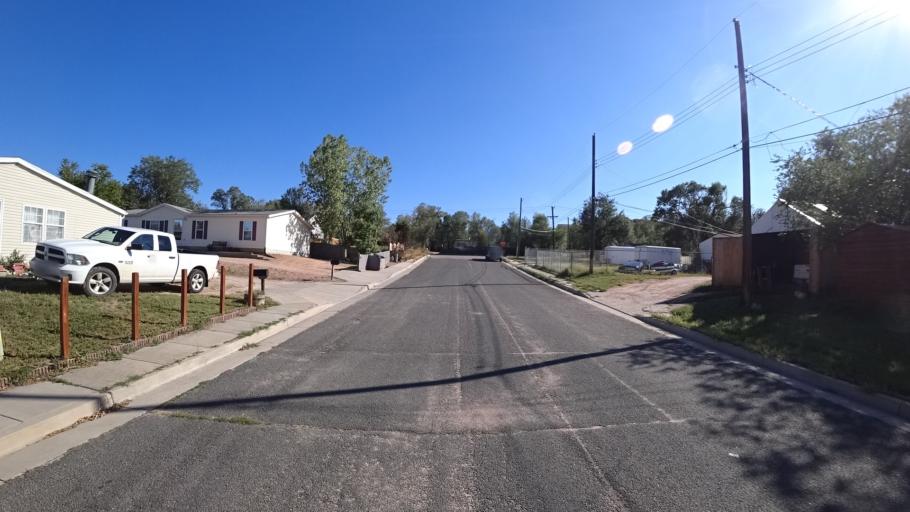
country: US
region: Colorado
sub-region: El Paso County
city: Colorado Springs
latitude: 38.8360
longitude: -104.8682
